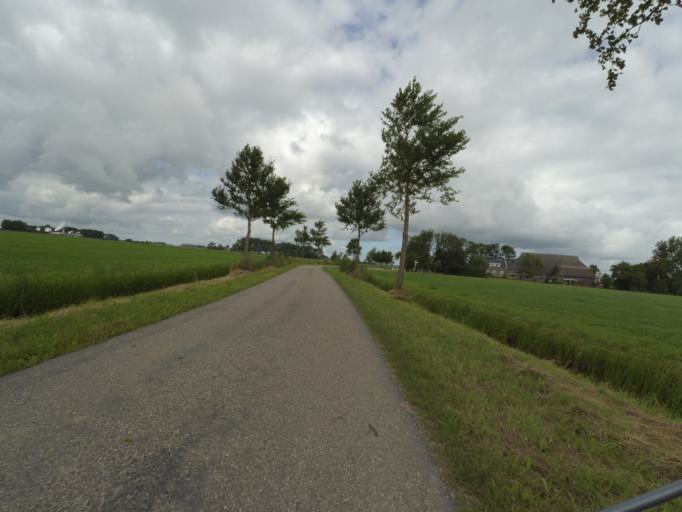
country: NL
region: Friesland
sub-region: Gemeente Kollumerland en Nieuwkruisland
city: Kollum
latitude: 53.2854
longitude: 6.2256
